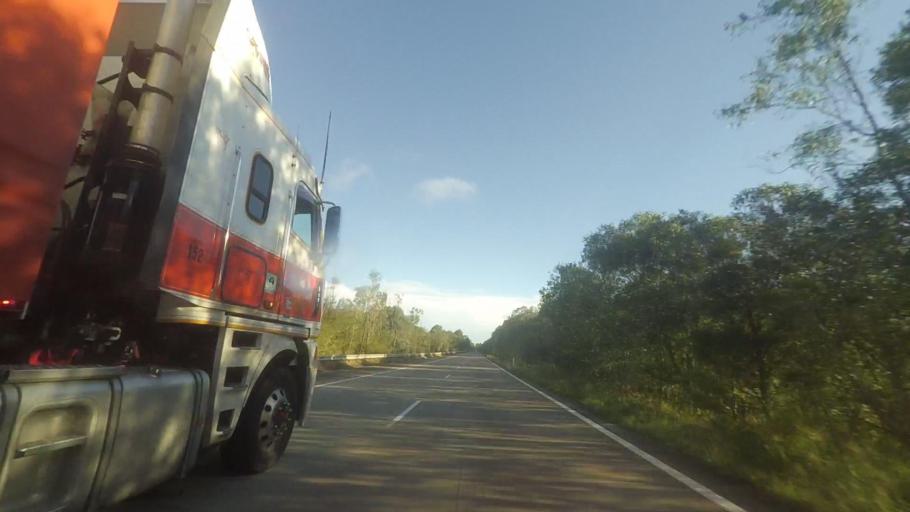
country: AU
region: New South Wales
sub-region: Great Lakes
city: Bulahdelah
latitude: -32.2904
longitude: 152.3424
